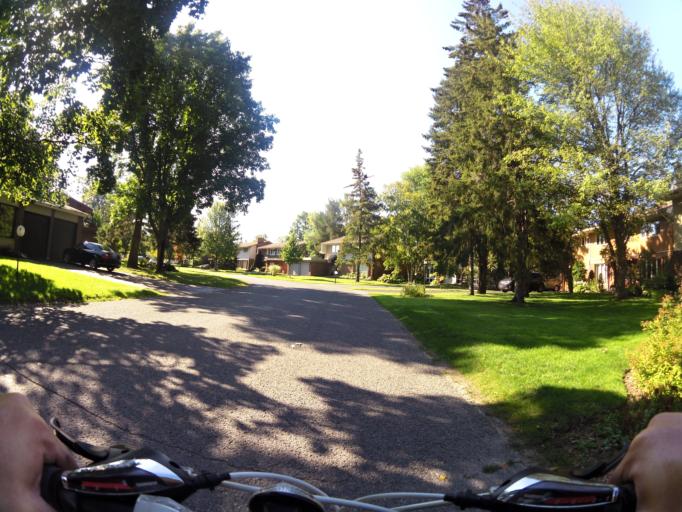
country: CA
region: Ontario
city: Bells Corners
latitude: 45.3311
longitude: -75.8968
